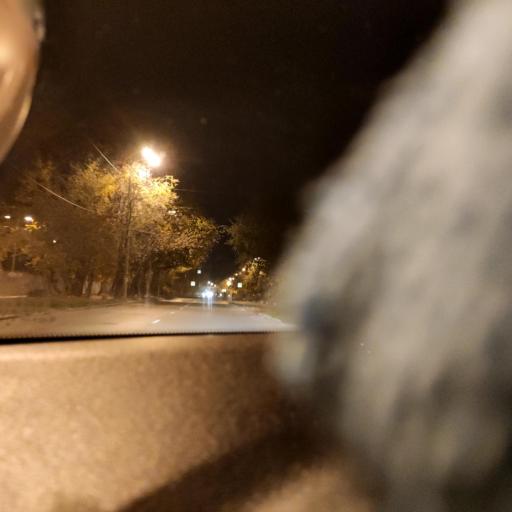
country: RU
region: Samara
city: Samara
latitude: 53.2145
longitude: 50.1959
